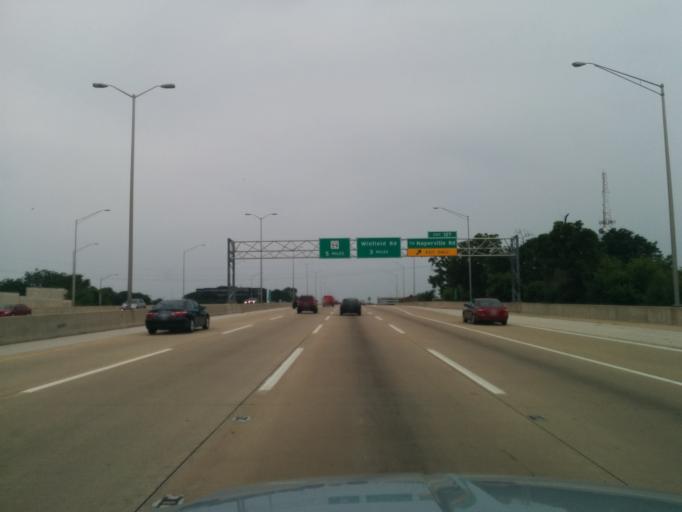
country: US
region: Illinois
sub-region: DuPage County
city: Naperville
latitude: 41.8061
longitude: -88.1166
